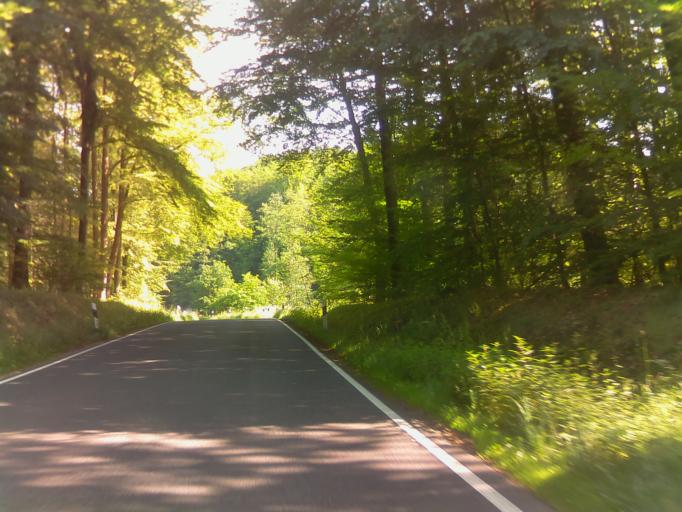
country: DE
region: Hesse
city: Beuern
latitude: 50.6451
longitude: 8.8325
